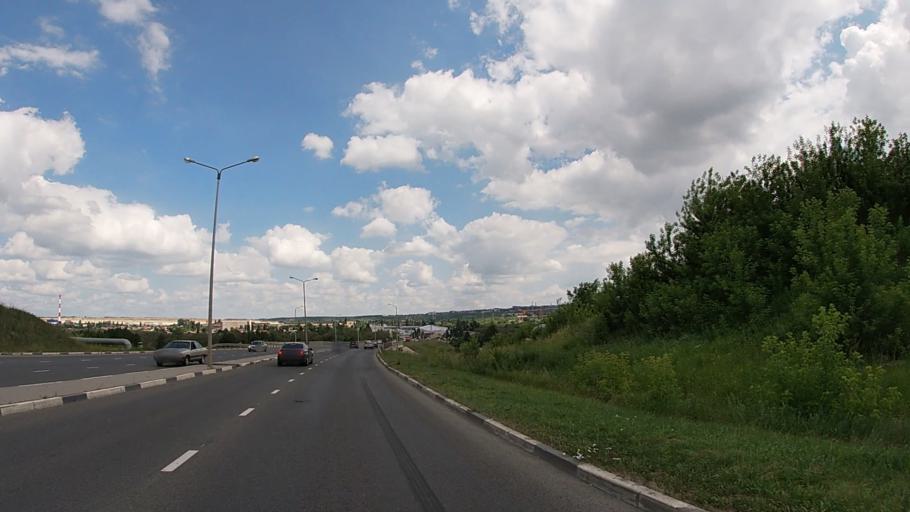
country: RU
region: Belgorod
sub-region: Belgorodskiy Rayon
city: Belgorod
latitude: 50.6050
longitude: 36.5303
